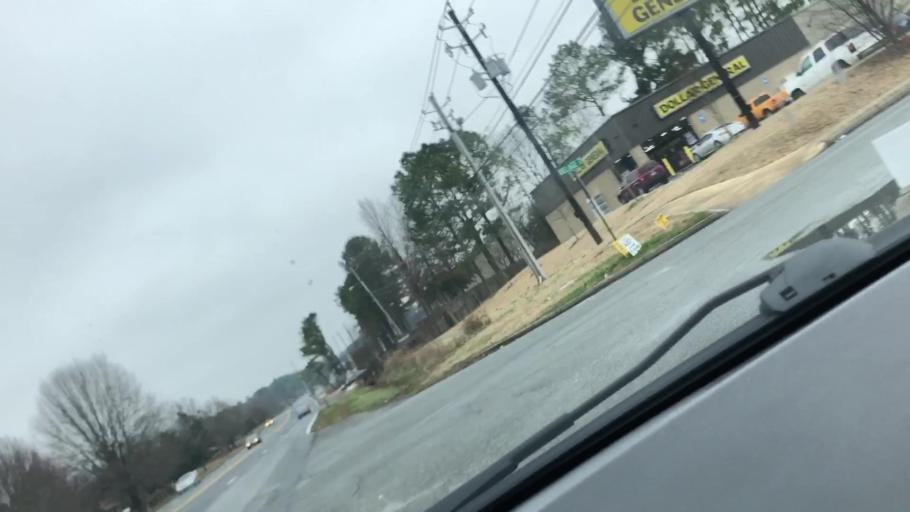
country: US
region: Georgia
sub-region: Bartow County
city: Cartersville
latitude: 34.2171
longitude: -84.8189
